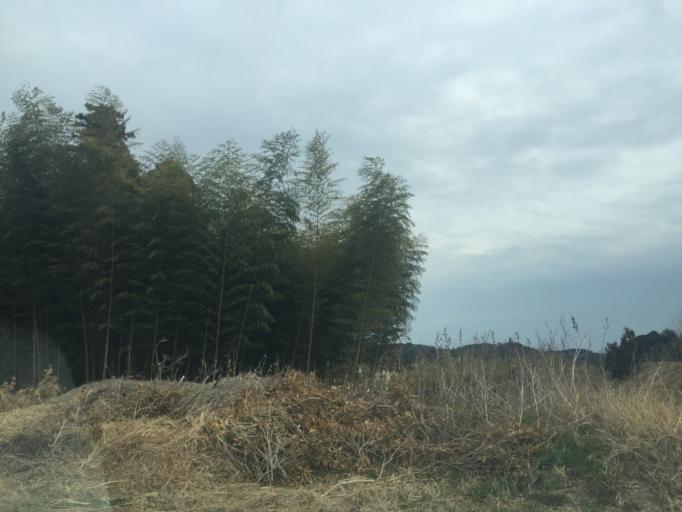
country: JP
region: Shizuoka
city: Kakegawa
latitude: 34.7900
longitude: 138.0644
